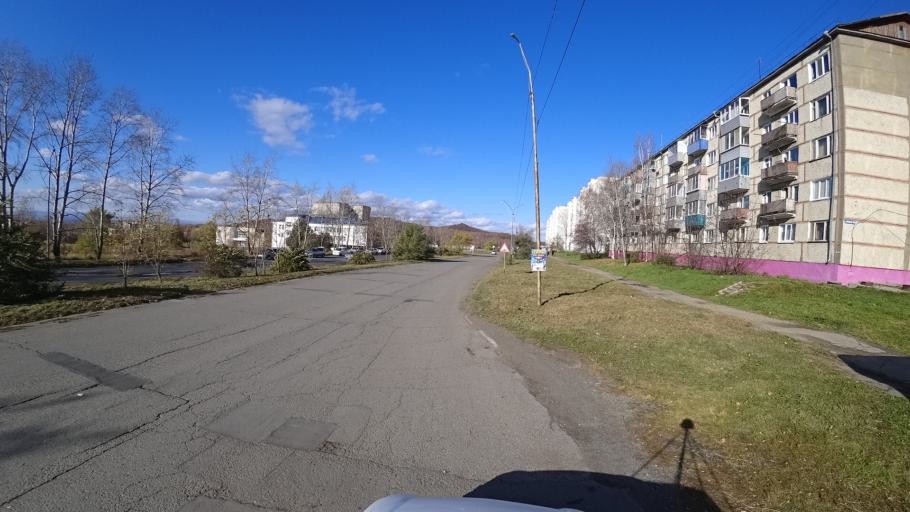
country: RU
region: Khabarovsk Krai
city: Amursk
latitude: 50.2457
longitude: 136.9160
